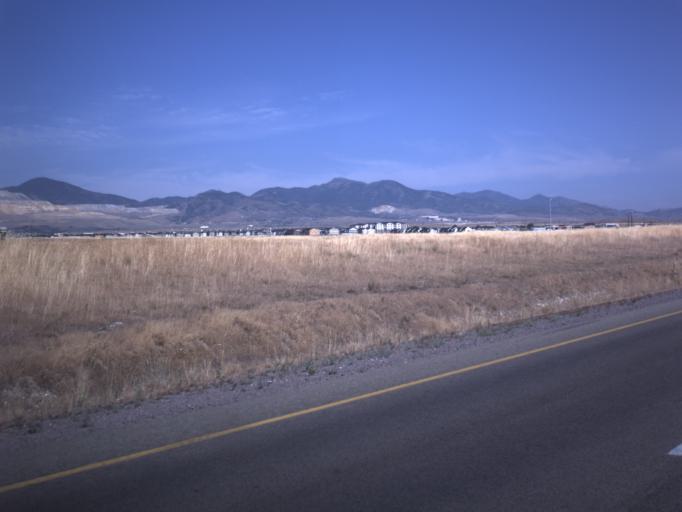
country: US
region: Utah
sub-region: Salt Lake County
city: Herriman
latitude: 40.5271
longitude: -112.0061
